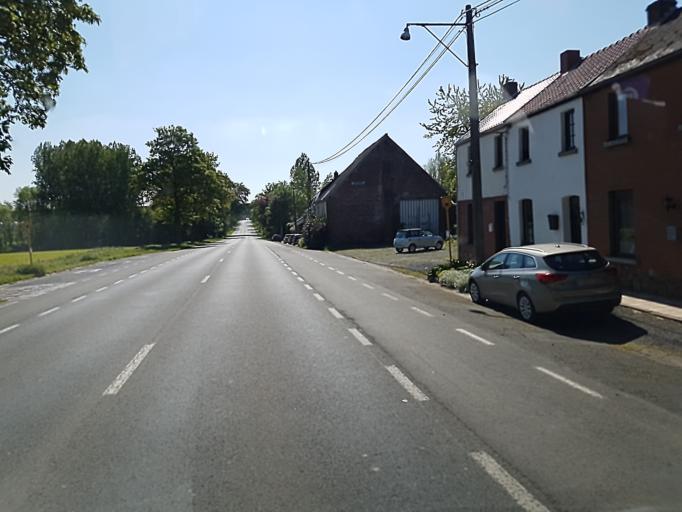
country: BE
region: Wallonia
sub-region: Province du Hainaut
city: Chievres
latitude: 50.6070
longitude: 3.8075
